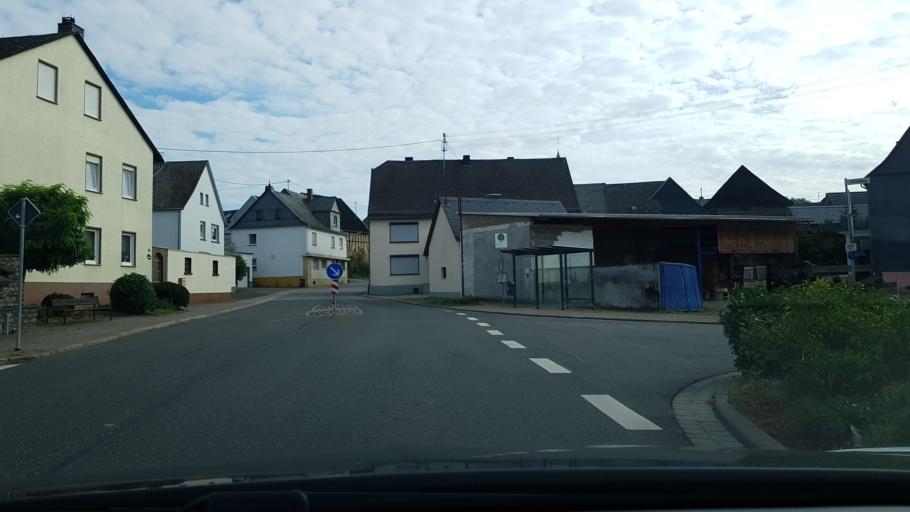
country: DE
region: Rheinland-Pfalz
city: Gondershausen
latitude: 50.1603
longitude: 7.4954
